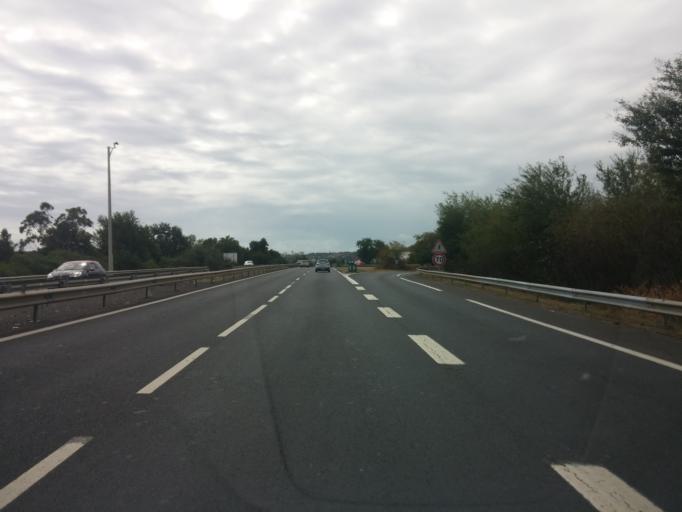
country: RE
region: Reunion
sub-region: Reunion
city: Saint-Paul
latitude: -20.9892
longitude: 55.2900
